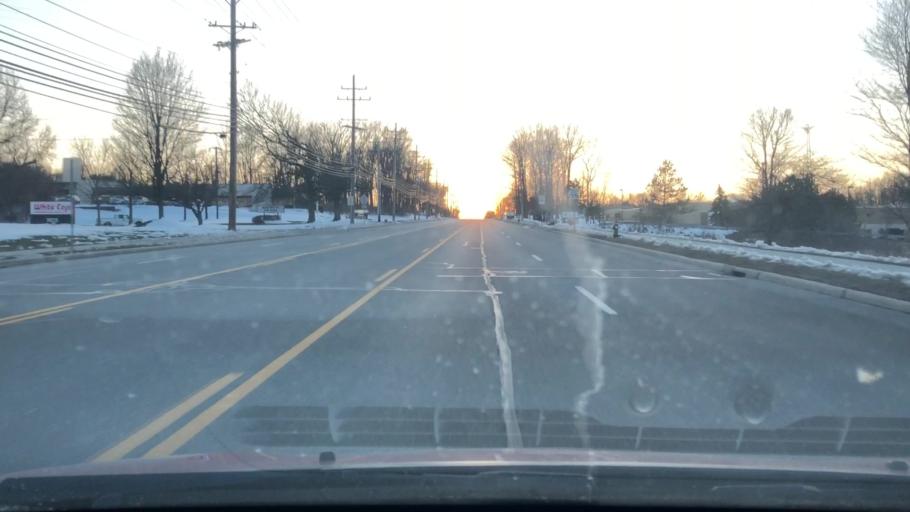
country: US
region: Ohio
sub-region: Cuyahoga County
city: Independence
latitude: 41.3621
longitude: -81.6266
